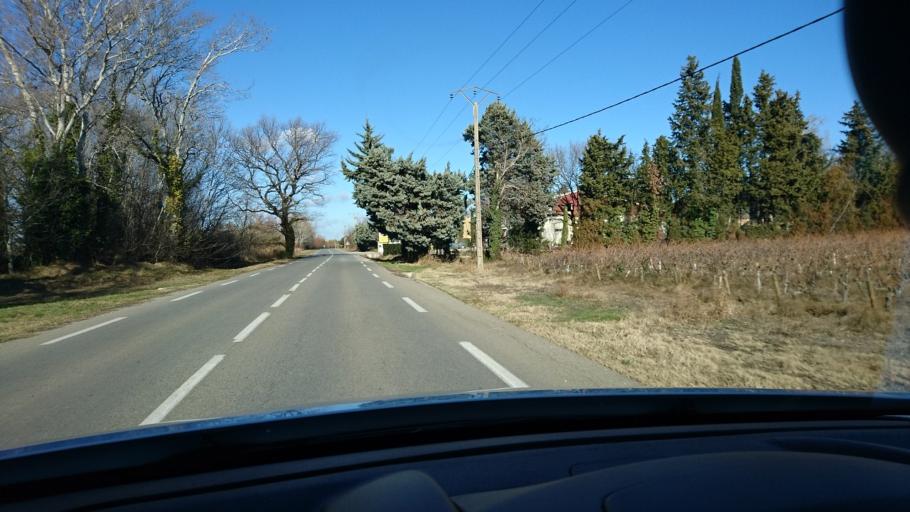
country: FR
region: Provence-Alpes-Cote d'Azur
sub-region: Departement du Vaucluse
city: Morieres-les-Avignon
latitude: 43.9188
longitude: 4.9063
